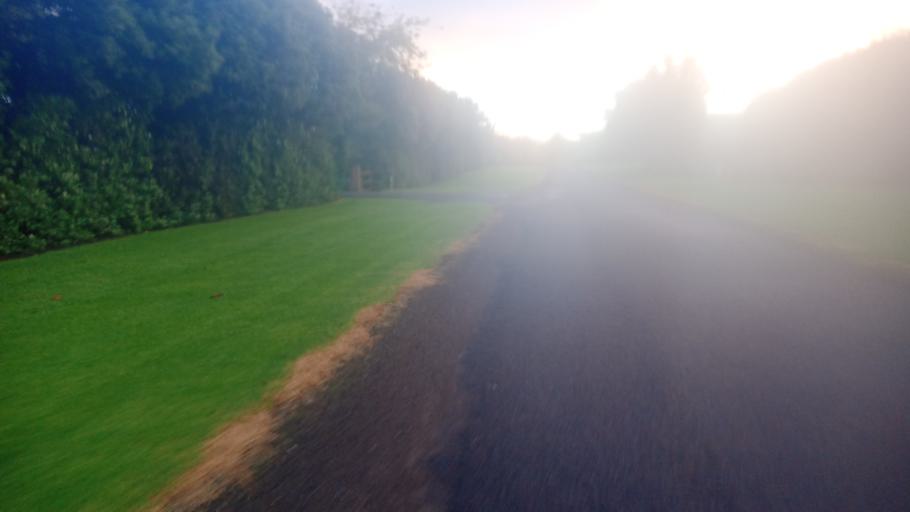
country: NZ
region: Gisborne
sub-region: Gisborne District
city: Gisborne
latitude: -38.6416
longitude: 177.9884
